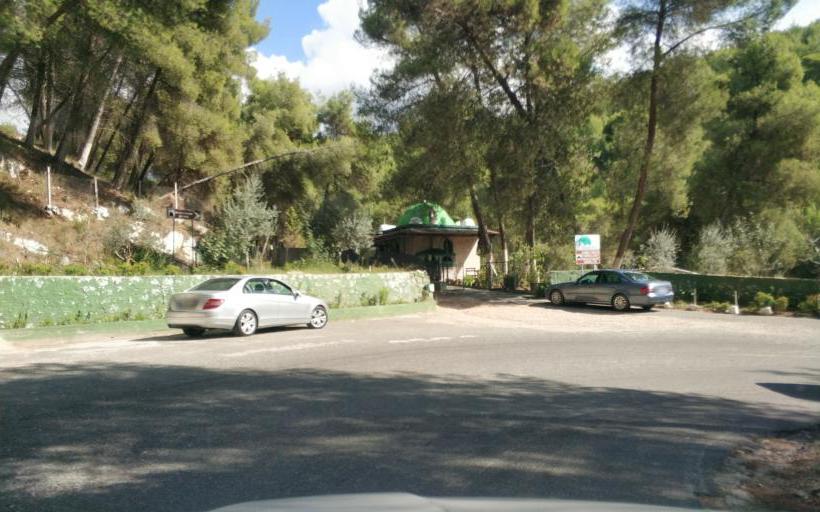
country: AL
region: Durres
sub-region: Rrethi i Krujes
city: Kruje
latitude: 41.4910
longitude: 19.7695
